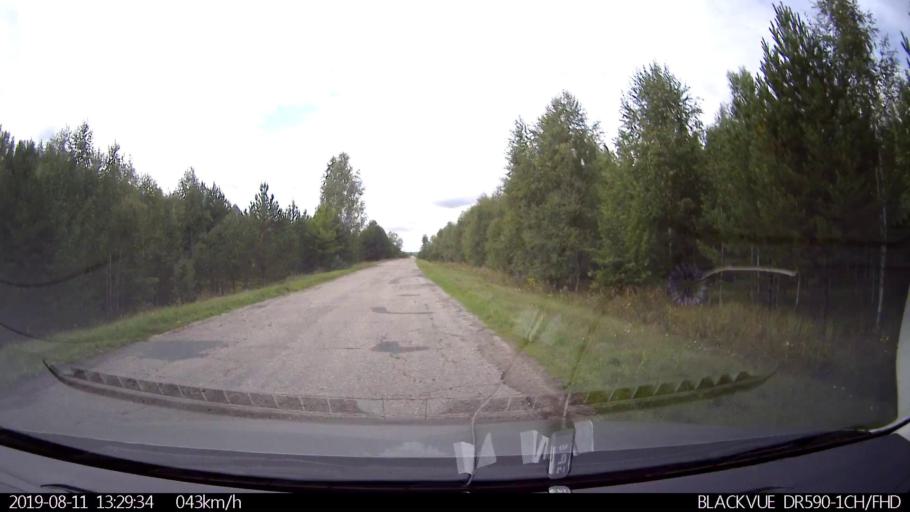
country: RU
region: Ulyanovsk
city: Ignatovka
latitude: 53.8597
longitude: 47.6133
